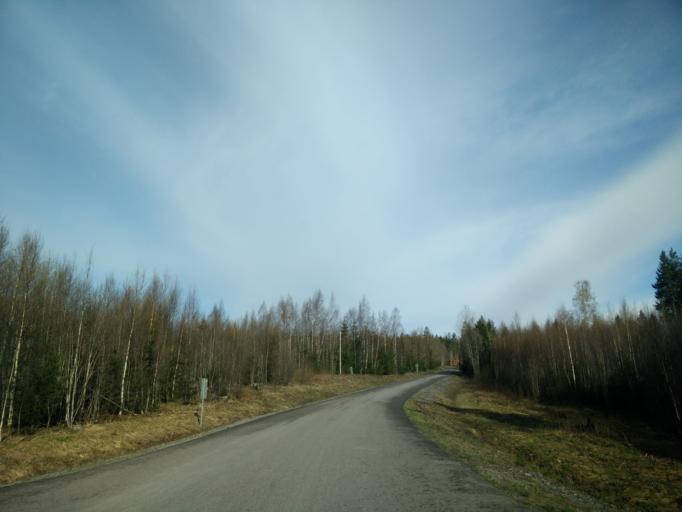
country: SE
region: Vaesternorrland
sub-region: Haernoesands Kommun
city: Haernoesand
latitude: 62.5869
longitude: 17.7682
